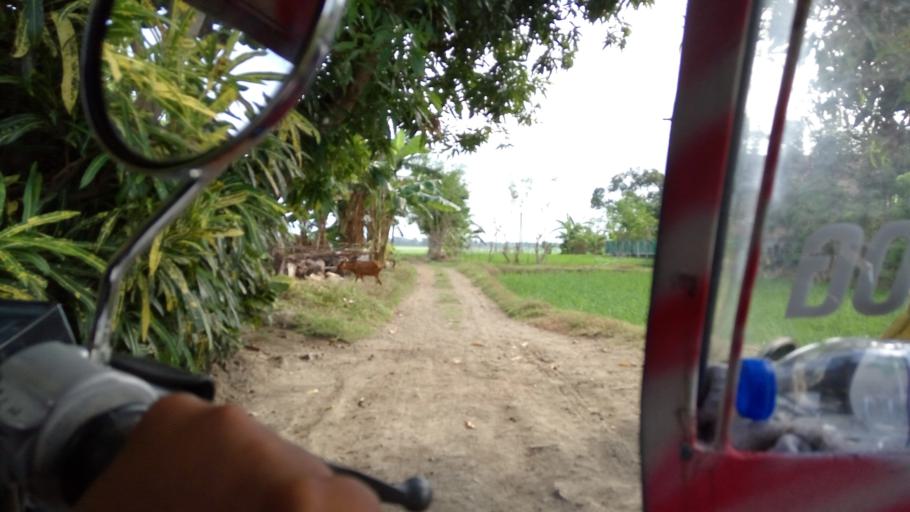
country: PH
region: Ilocos
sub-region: Province of La Union
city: San Eugenio
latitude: 16.3530
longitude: 120.3527
